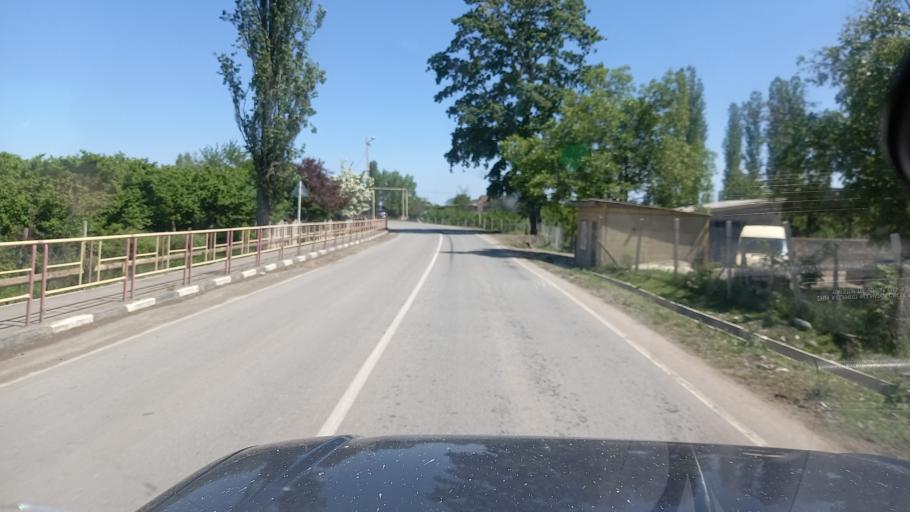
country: RU
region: Dagestan
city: Samur
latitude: 41.7589
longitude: 48.4876
